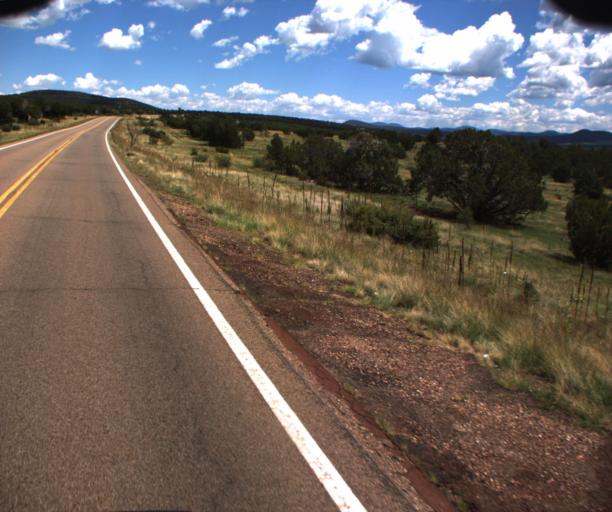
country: US
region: Arizona
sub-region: Navajo County
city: White Mountain Lake
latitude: 34.2861
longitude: -109.8269
